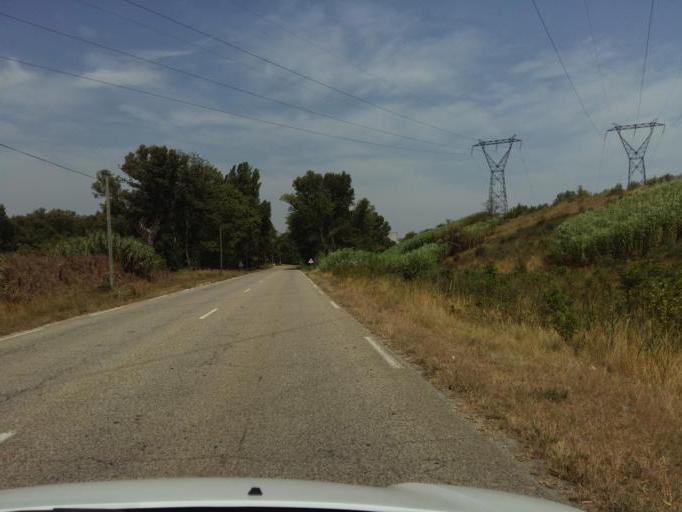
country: FR
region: Provence-Alpes-Cote d'Azur
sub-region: Departement du Vaucluse
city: Bollene
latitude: 44.3061
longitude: 4.7375
